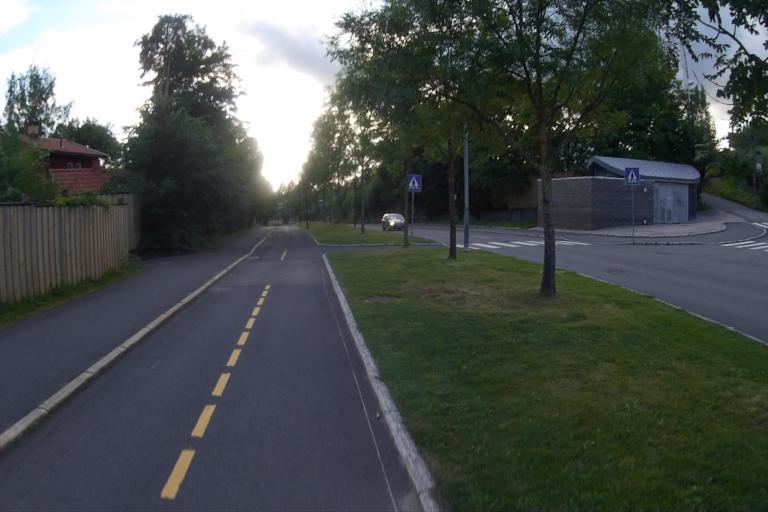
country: NO
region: Oslo
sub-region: Oslo
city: Oslo
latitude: 59.9531
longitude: 10.7570
